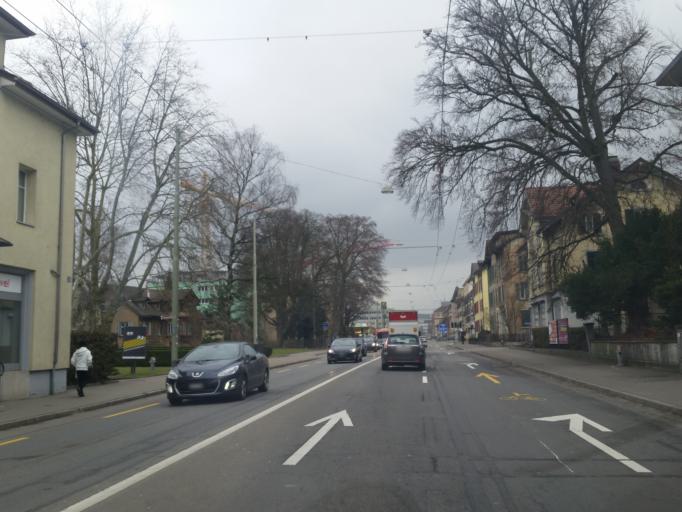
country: CH
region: Zurich
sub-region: Bezirk Winterthur
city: Stadt Winterthur (Kreis 1) / Bruehlberg
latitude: 47.4931
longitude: 8.7093
